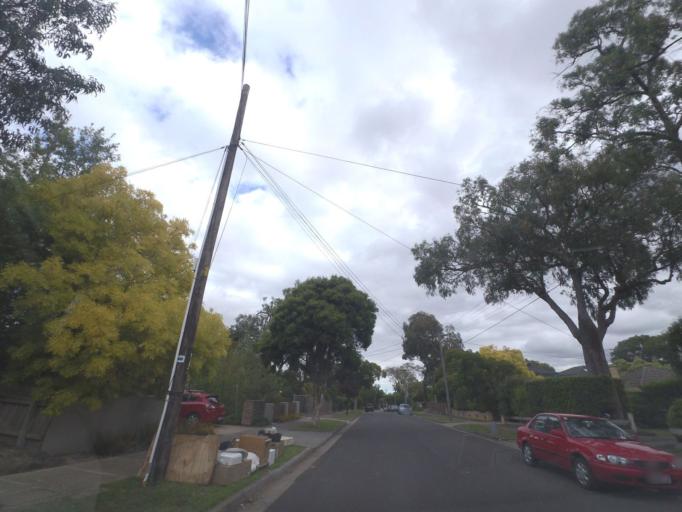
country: AU
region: Victoria
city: Mitcham
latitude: -37.8213
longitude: 145.2062
